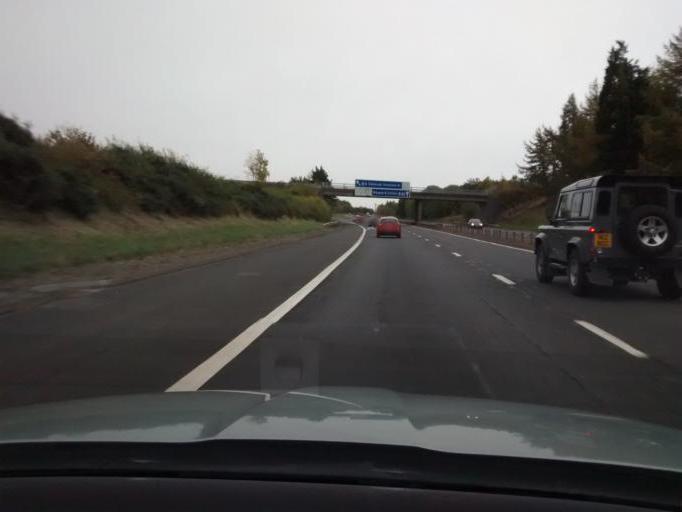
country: GB
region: Scotland
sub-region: Stirling
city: Bannockburn
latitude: 56.0833
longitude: -3.9385
